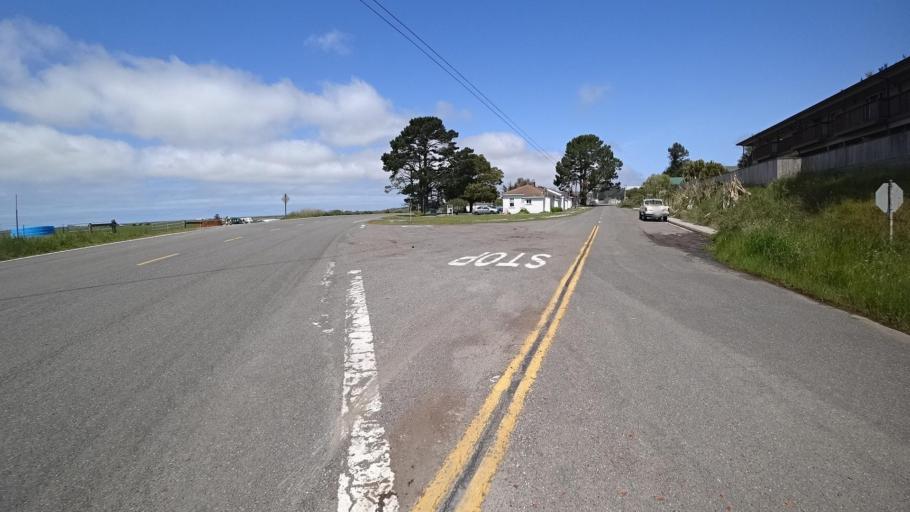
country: US
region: California
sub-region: Humboldt County
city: Ferndale
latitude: 40.6382
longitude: -124.2254
